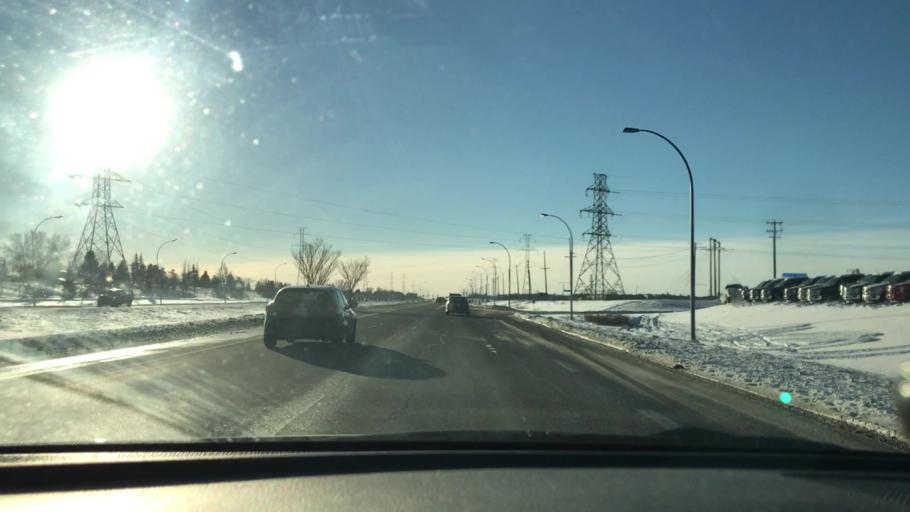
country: CA
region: Alberta
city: Edmonton
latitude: 53.4637
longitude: -113.4668
